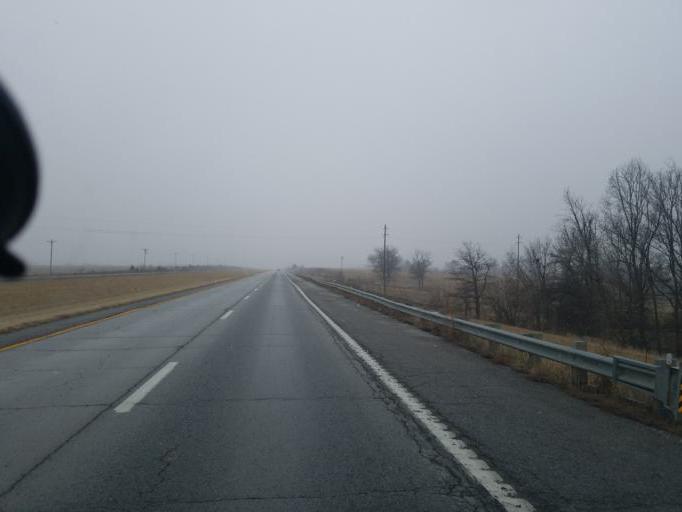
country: US
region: Missouri
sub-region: Macon County
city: La Plata
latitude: 39.9632
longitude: -92.4765
